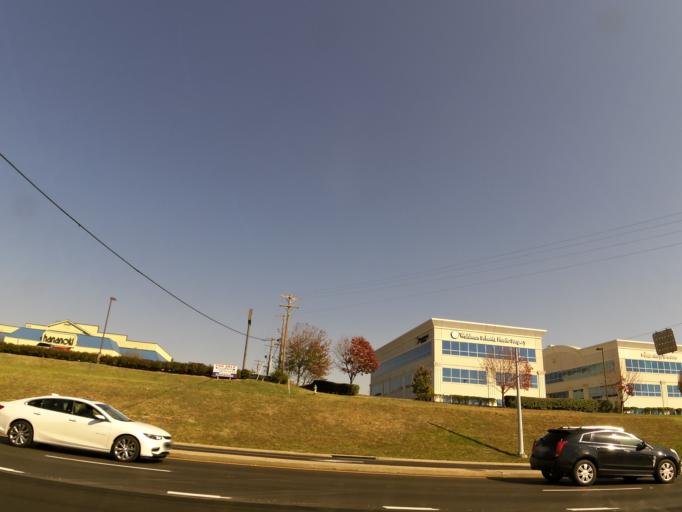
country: US
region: Kentucky
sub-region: Fayette County
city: Lexington
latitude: 37.9994
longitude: -84.4444
